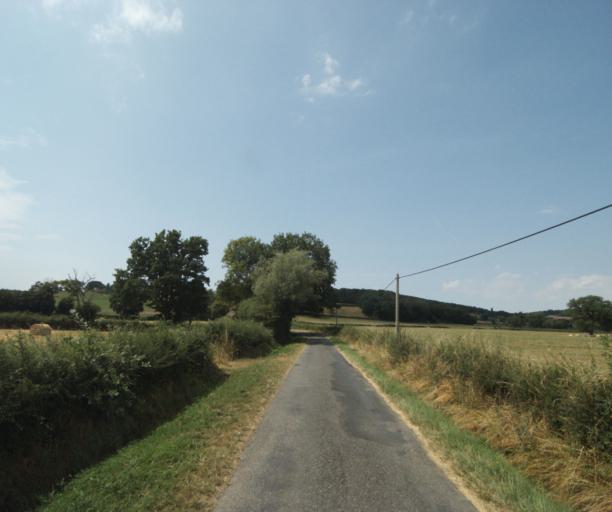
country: FR
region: Bourgogne
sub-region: Departement de Saone-et-Loire
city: Gueugnon
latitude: 46.6007
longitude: 4.0452
